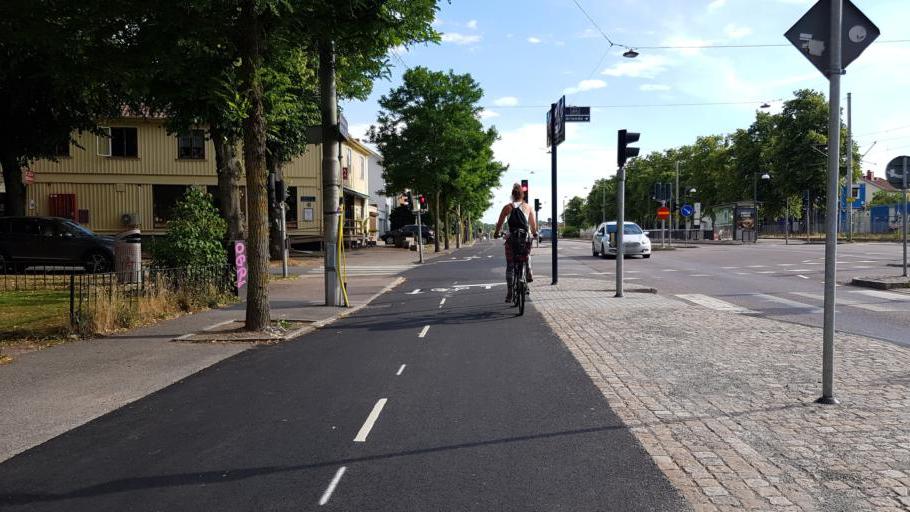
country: SE
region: Vaestra Goetaland
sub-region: Goteborg
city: Goeteborg
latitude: 57.7137
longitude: 12.0246
